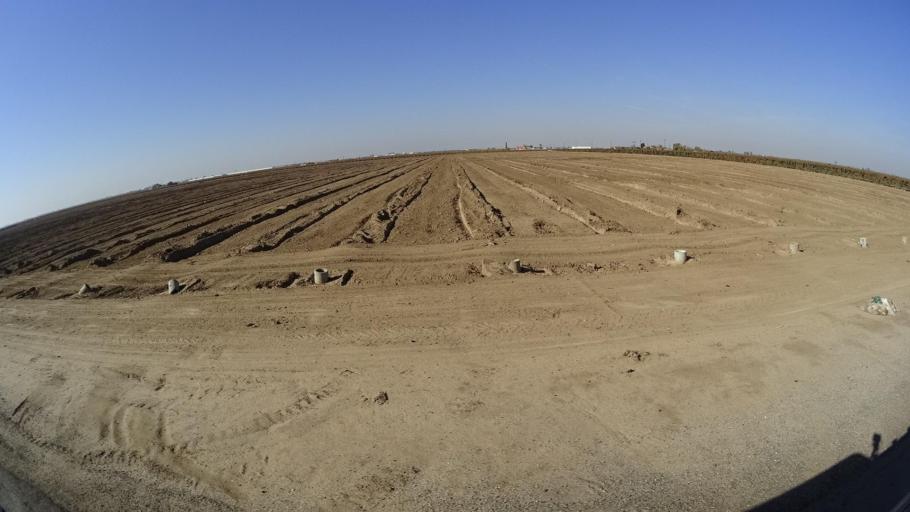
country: US
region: California
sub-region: Kern County
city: Delano
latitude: 35.7380
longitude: -119.2052
